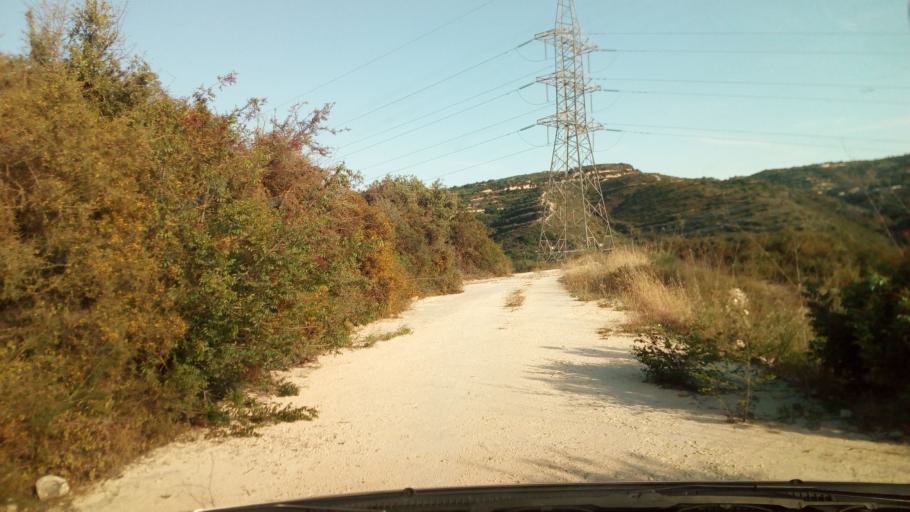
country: CY
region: Pafos
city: Tala
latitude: 34.8728
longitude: 32.4620
